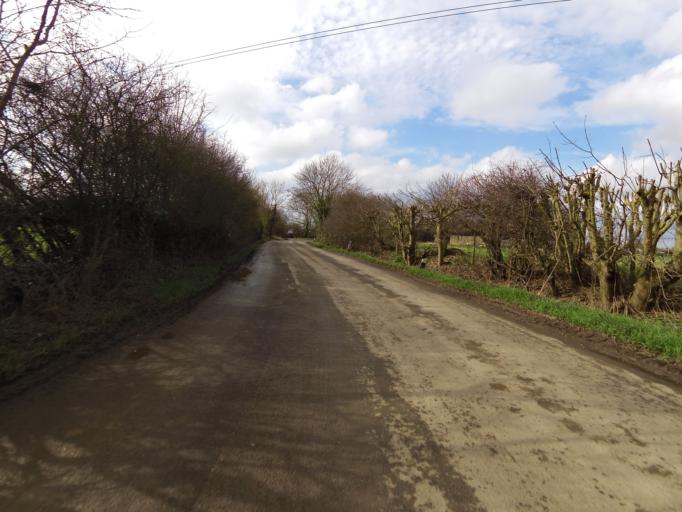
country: GB
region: England
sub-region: Doncaster
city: Moss
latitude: 53.6003
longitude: -1.0901
